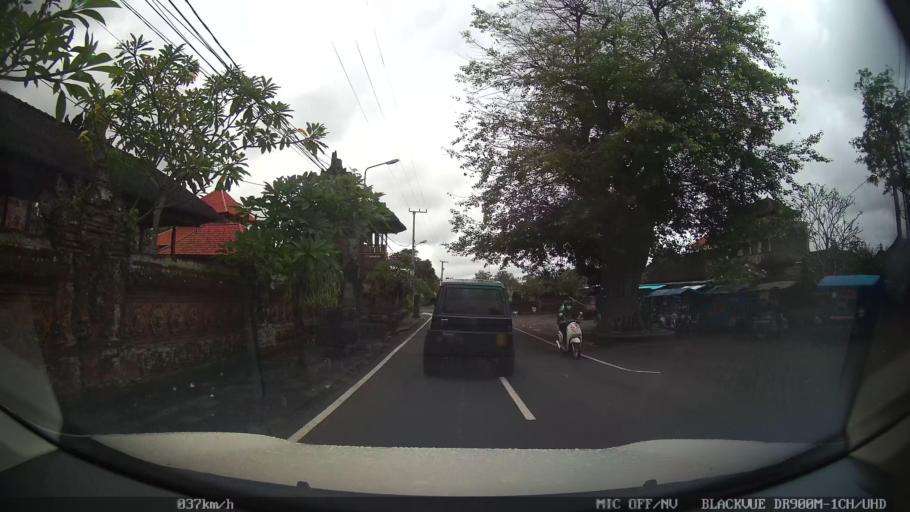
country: ID
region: Bali
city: Banjar Sayanbaleran
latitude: -8.5190
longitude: 115.1871
